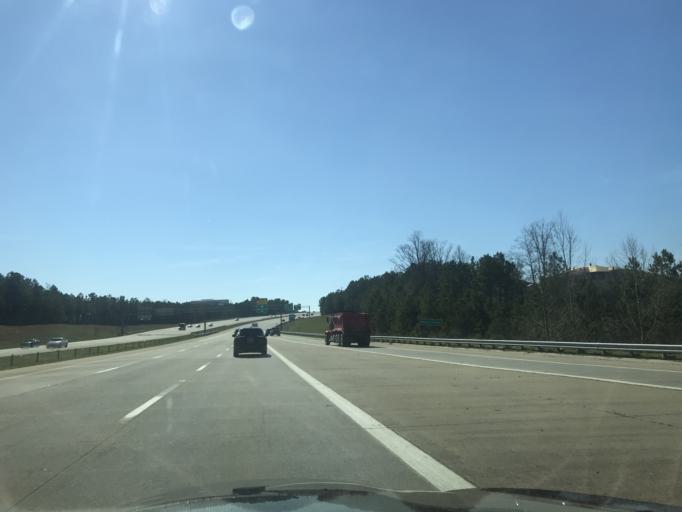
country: US
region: North Carolina
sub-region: Wake County
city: Morrisville
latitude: 35.8675
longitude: -78.8357
